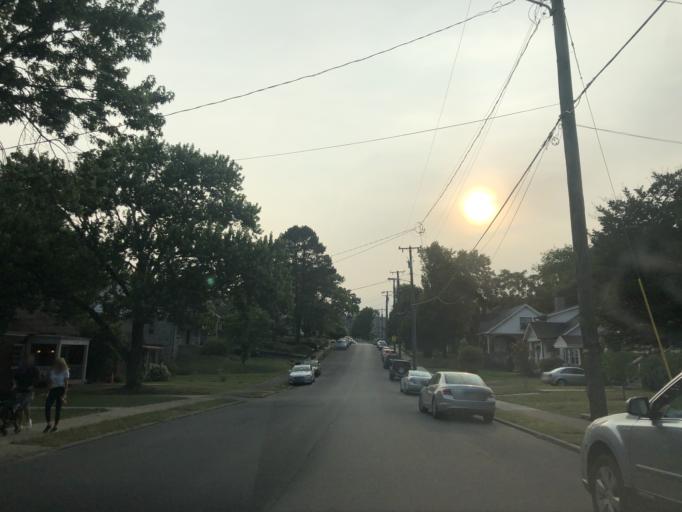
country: US
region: Tennessee
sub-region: Davidson County
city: Oak Hill
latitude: 36.1266
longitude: -86.7836
